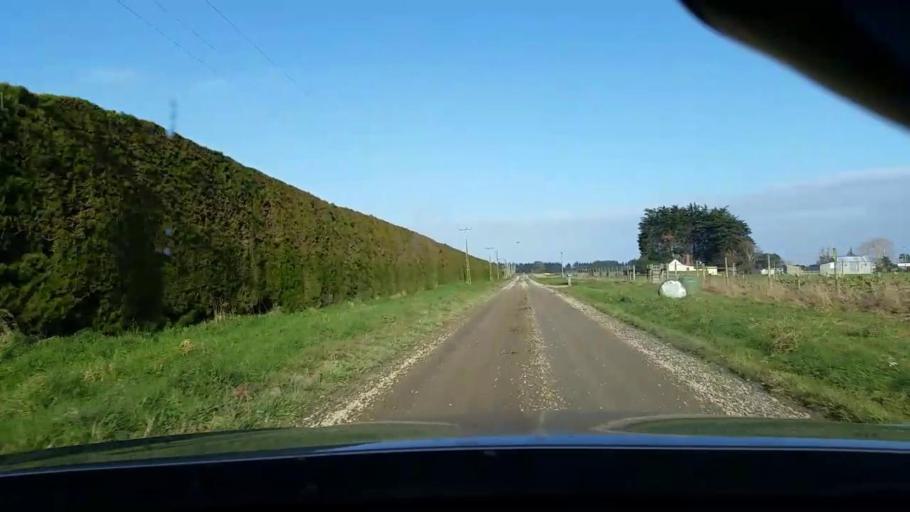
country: NZ
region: Southland
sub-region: Invercargill City
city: Invercargill
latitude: -46.2882
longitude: 168.2947
